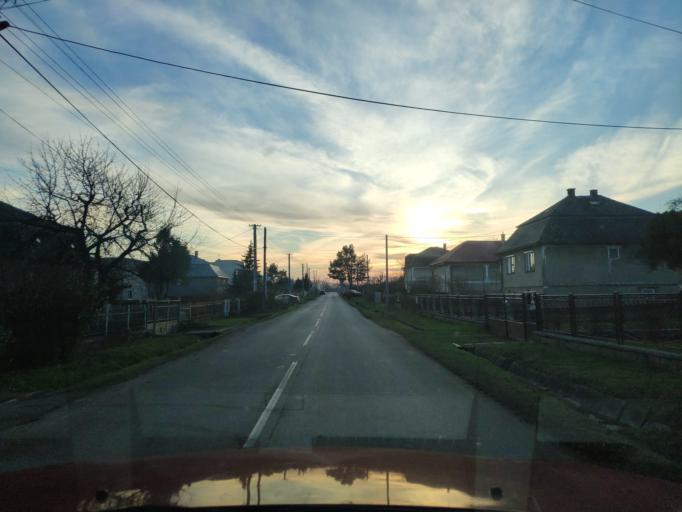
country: SK
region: Kosicky
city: Kosice
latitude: 48.6645
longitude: 21.3970
